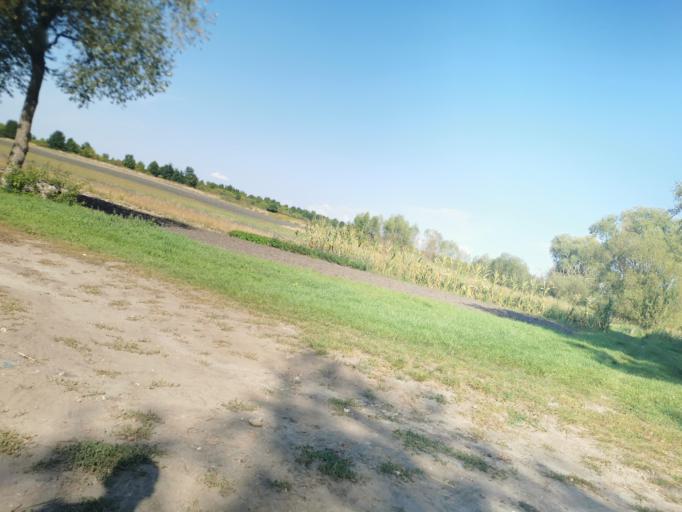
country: SK
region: Trnavsky
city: Gbely
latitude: 48.6207
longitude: 17.2232
